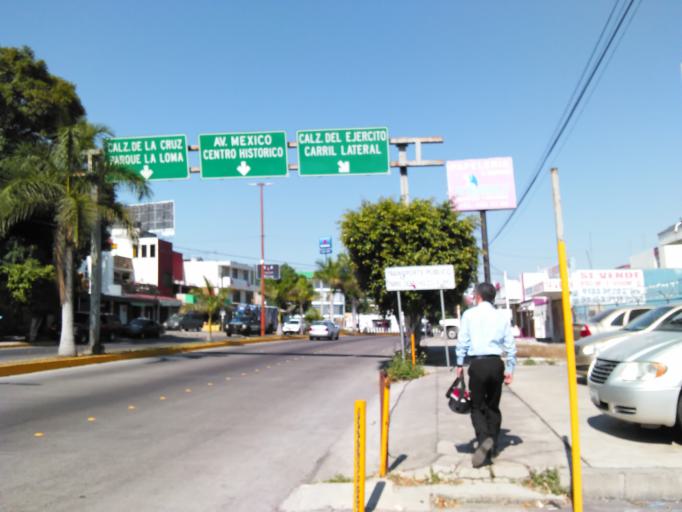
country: MX
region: Nayarit
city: Tepic
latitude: 21.4965
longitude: -104.8970
